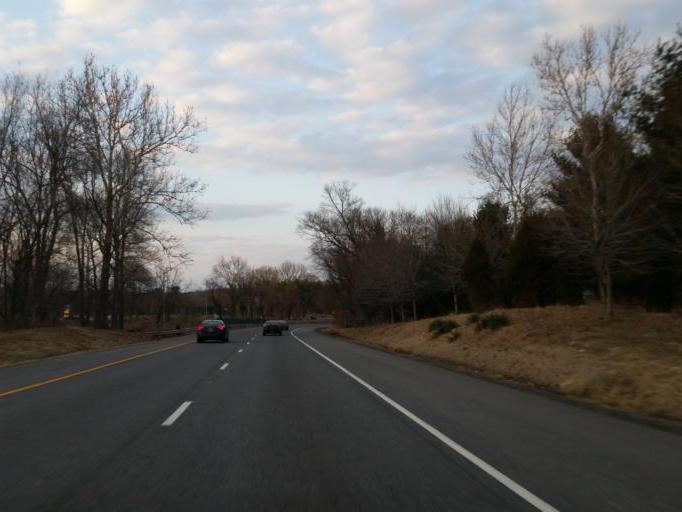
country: US
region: Maryland
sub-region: Baltimore County
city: Mays Chapel
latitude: 39.4102
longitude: -76.6620
